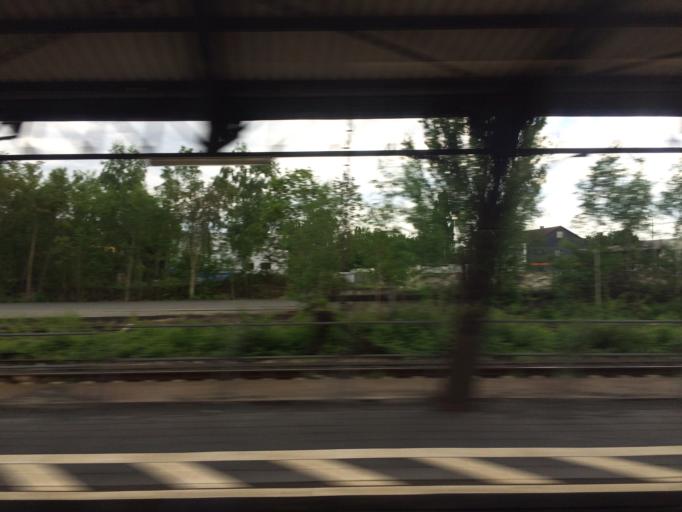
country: DE
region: Hesse
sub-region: Regierungsbezirk Darmstadt
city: Offenbach
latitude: 50.1354
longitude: 8.7692
